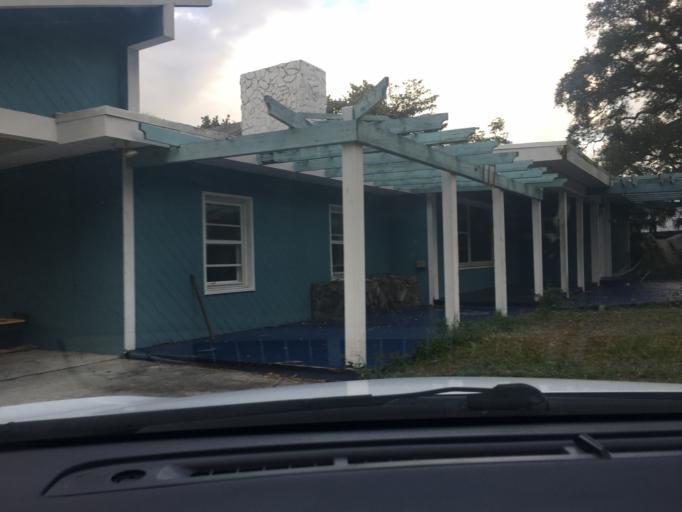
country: US
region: Florida
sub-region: Broward County
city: Dania Beach
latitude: 26.0675
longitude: -80.1800
